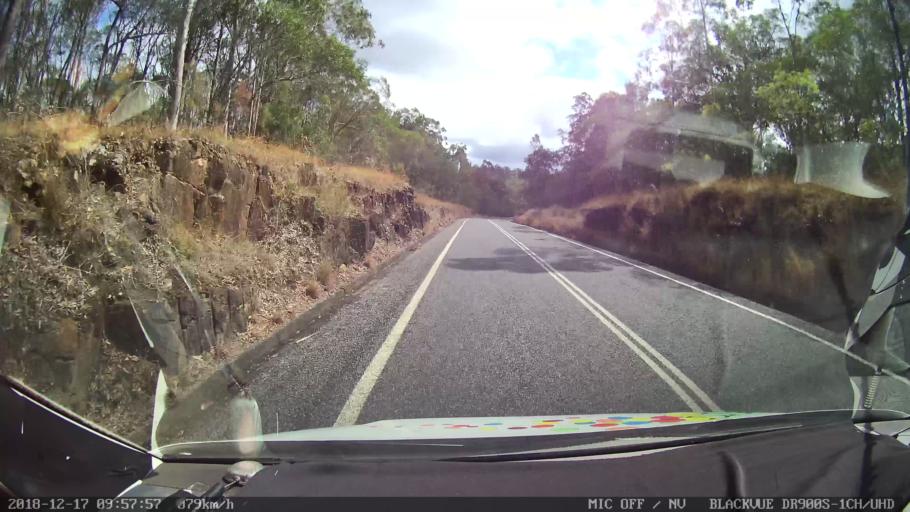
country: AU
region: New South Wales
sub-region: Tenterfield Municipality
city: Carrolls Creek
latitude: -28.9226
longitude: 152.4033
